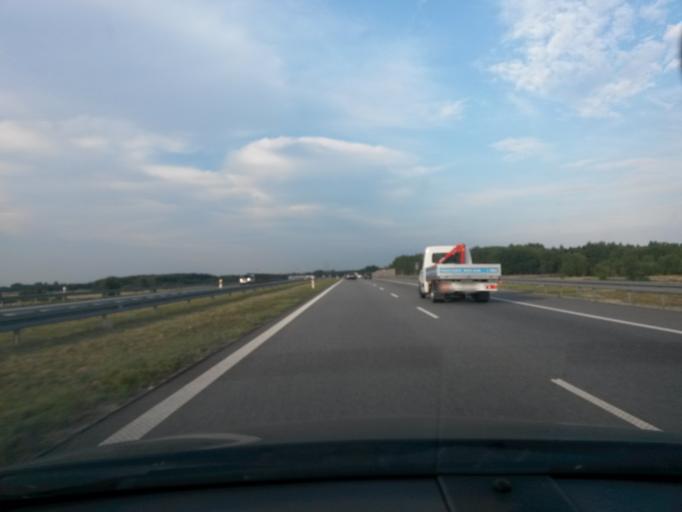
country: PL
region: Lodz Voivodeship
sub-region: powiat Lowicki
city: Bobrowniki
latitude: 52.0201
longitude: 19.9842
